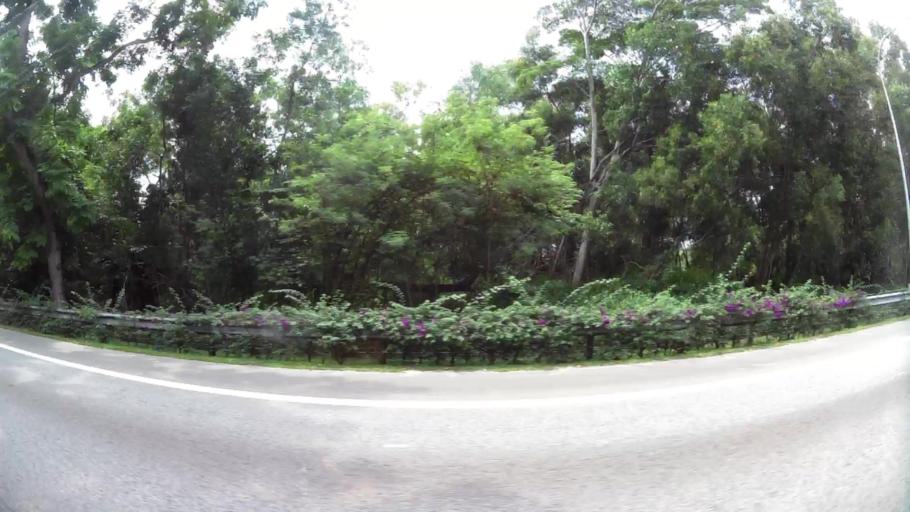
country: SG
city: Singapore
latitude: 1.3658
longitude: 103.9516
